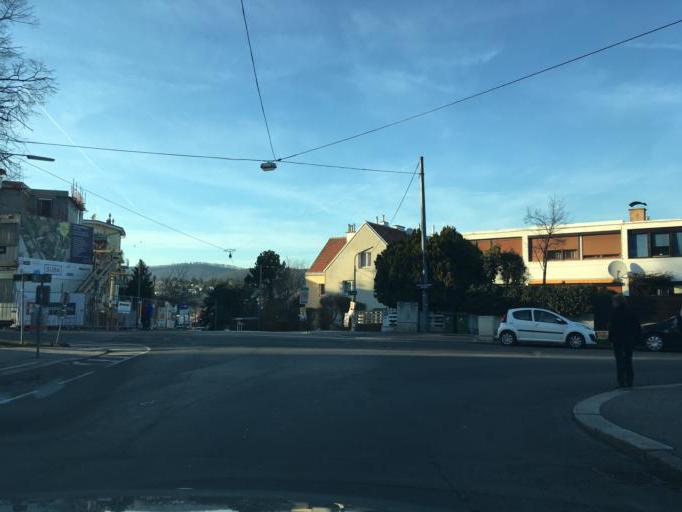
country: AT
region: Vienna
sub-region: Wien Stadt
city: Vienna
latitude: 48.2398
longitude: 16.3257
